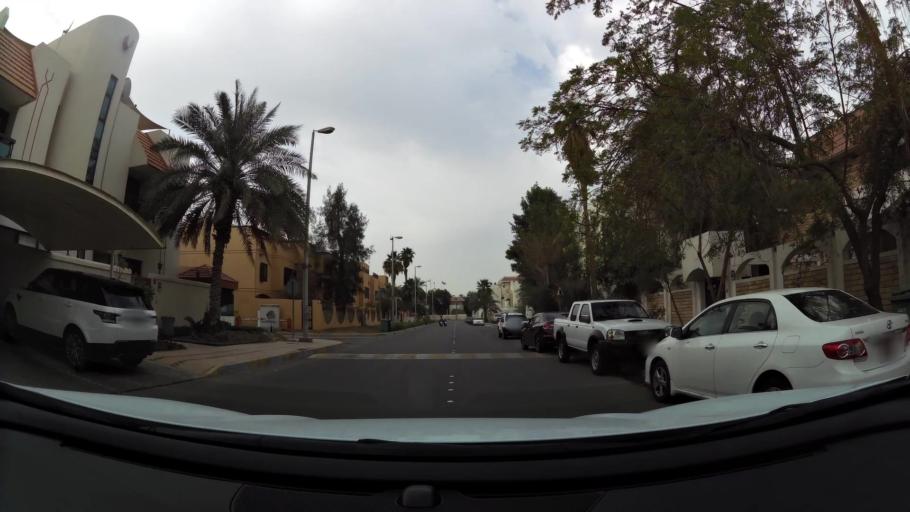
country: AE
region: Abu Dhabi
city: Abu Dhabi
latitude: 24.4629
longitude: 54.3712
